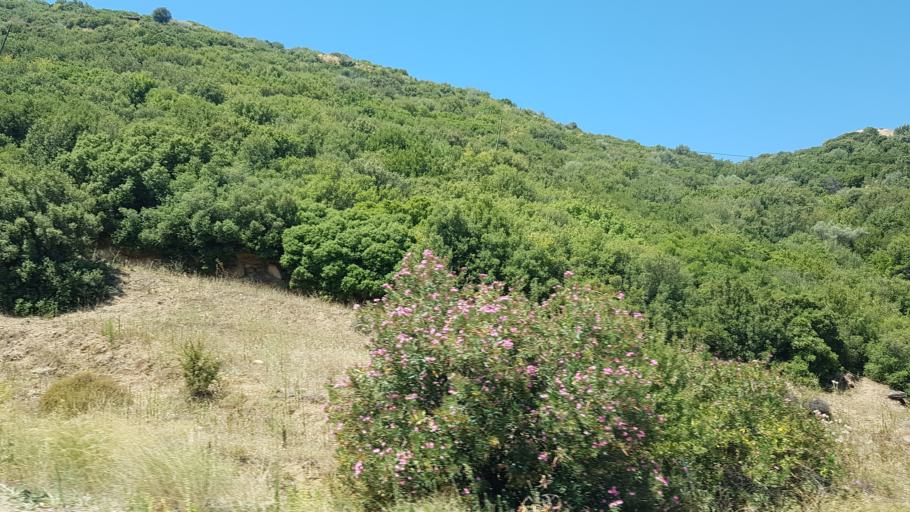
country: TR
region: Aydin
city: Akcaova
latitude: 37.5049
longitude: 28.1028
